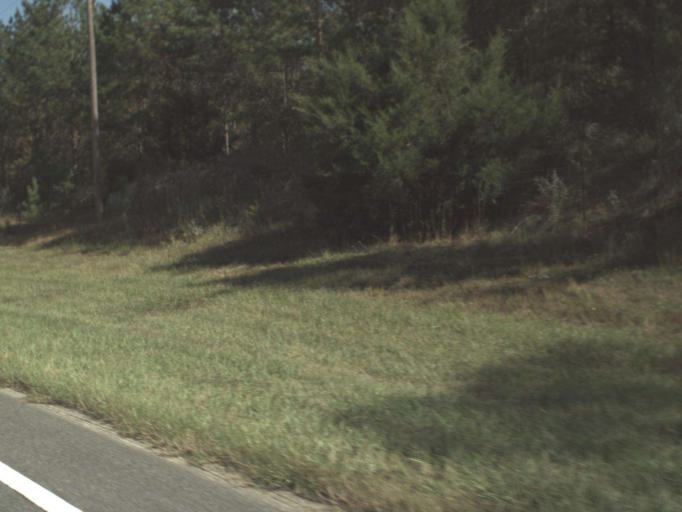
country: US
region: Alabama
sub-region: Geneva County
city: Samson
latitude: 30.9826
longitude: -85.9976
